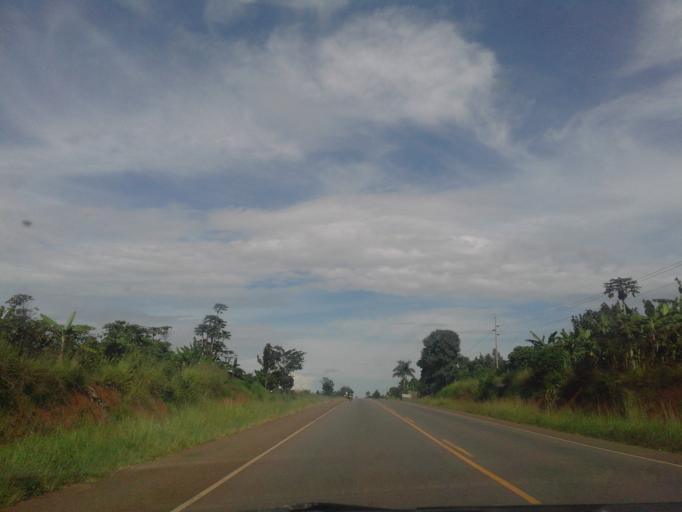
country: UG
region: Central Region
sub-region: Lwengo District
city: Lwengo
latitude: -0.3692
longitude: 31.5318
